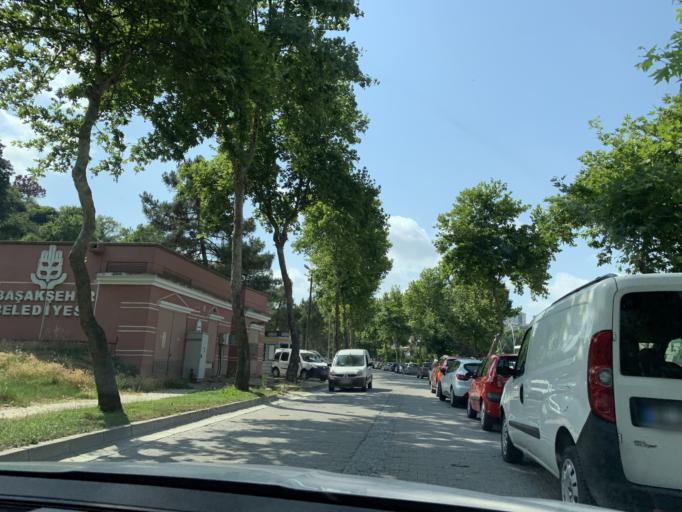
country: TR
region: Istanbul
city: Esenyurt
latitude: 41.0658
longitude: 28.6937
